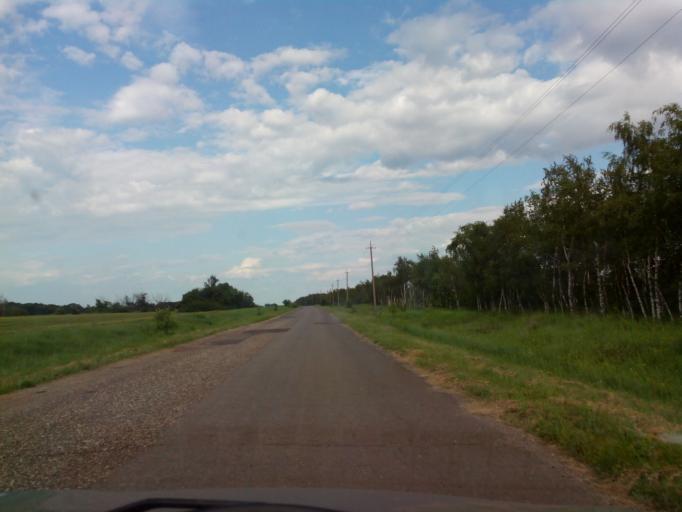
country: RU
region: Volgograd
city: Slashchevskaya
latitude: 49.7941
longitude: 42.3857
